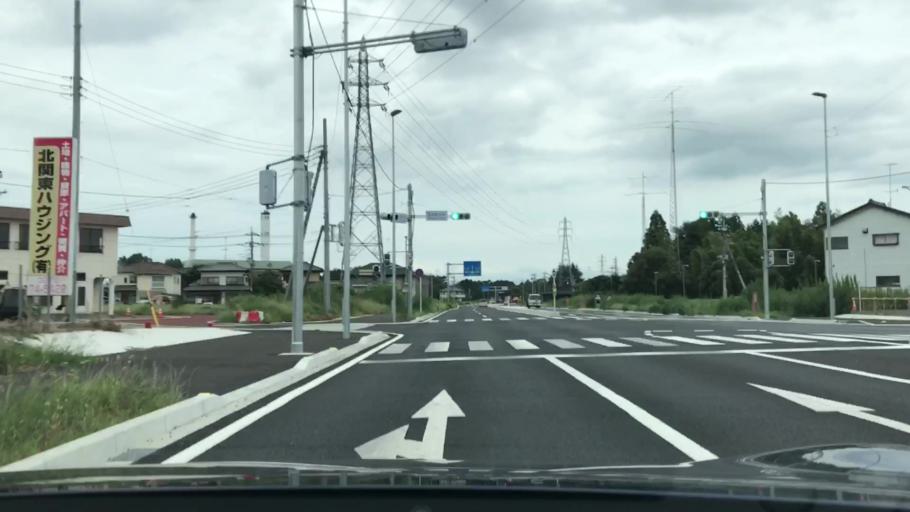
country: JP
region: Gunma
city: Tatebayashi
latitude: 36.2290
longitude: 139.5101
